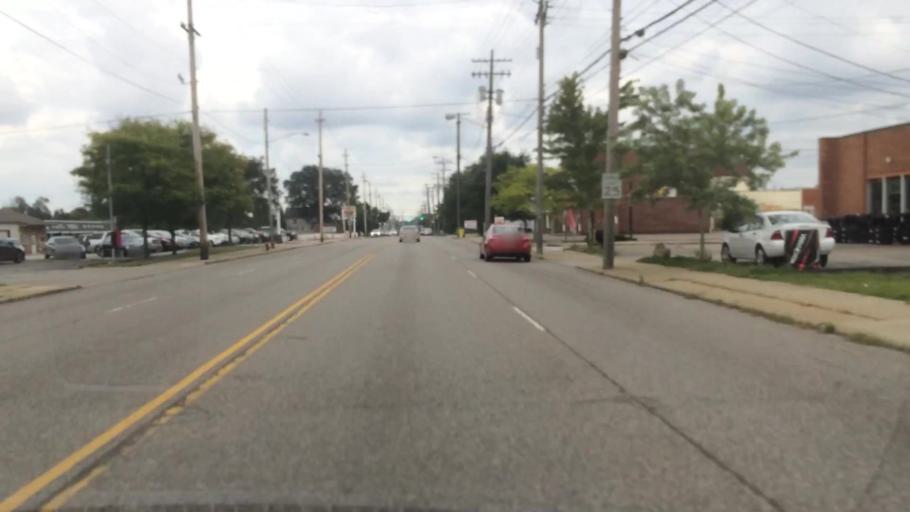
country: US
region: Ohio
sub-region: Cuyahoga County
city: Maple Heights
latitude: 41.4078
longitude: -81.5596
